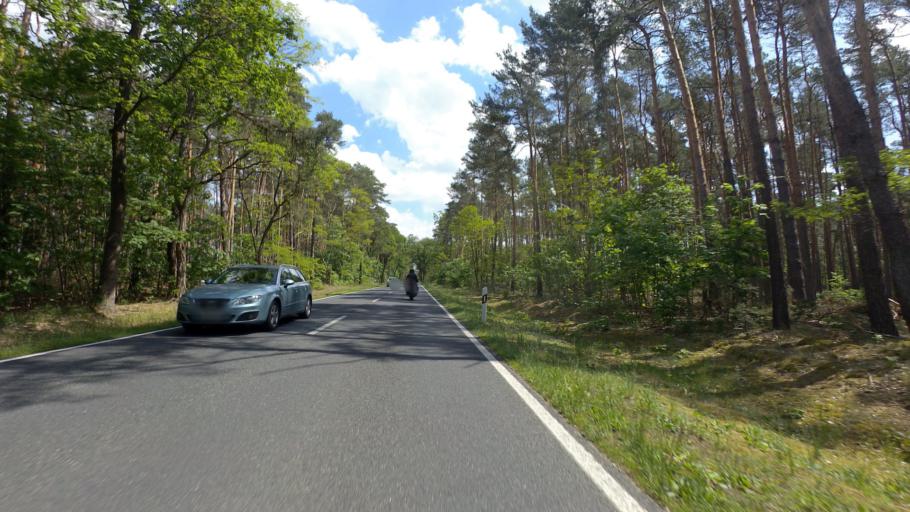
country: DE
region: Brandenburg
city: Lubbenau
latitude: 51.9438
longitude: 13.9951
